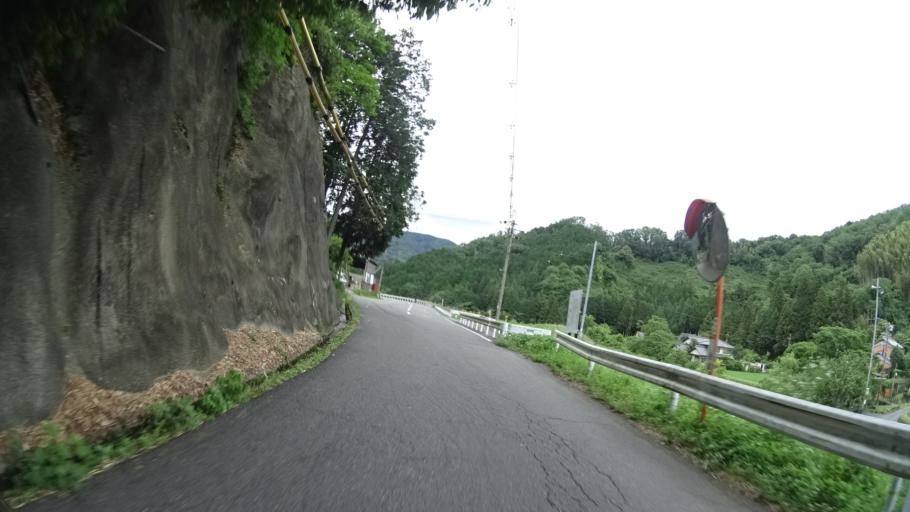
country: JP
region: Nara
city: Nara-shi
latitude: 34.7505
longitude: 135.9269
